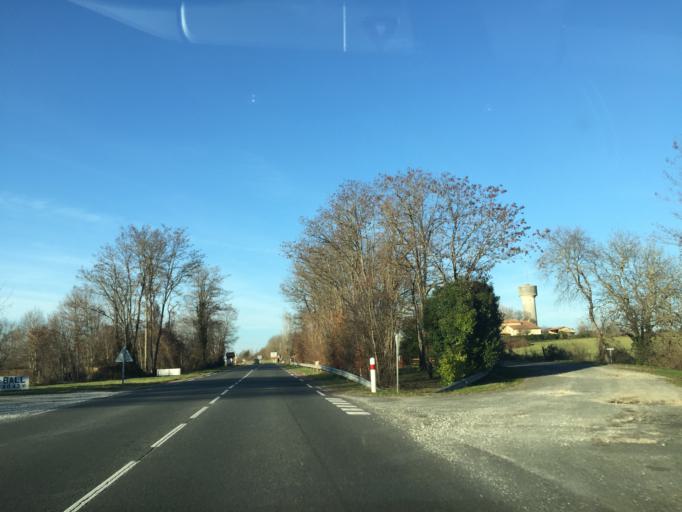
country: FR
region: Aquitaine
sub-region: Departement de la Dordogne
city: Riberac
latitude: 45.1954
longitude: 0.3692
